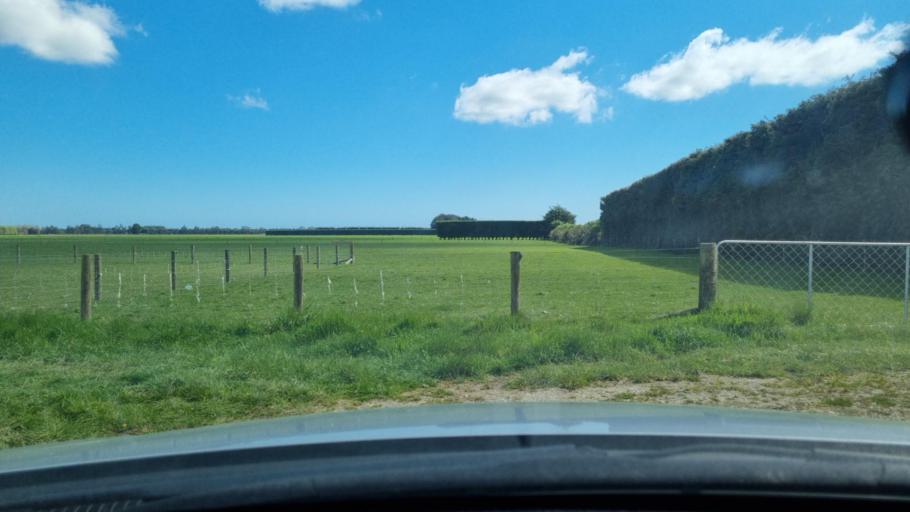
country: NZ
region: Southland
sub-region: Invercargill City
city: Invercargill
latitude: -46.3602
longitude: 168.3010
